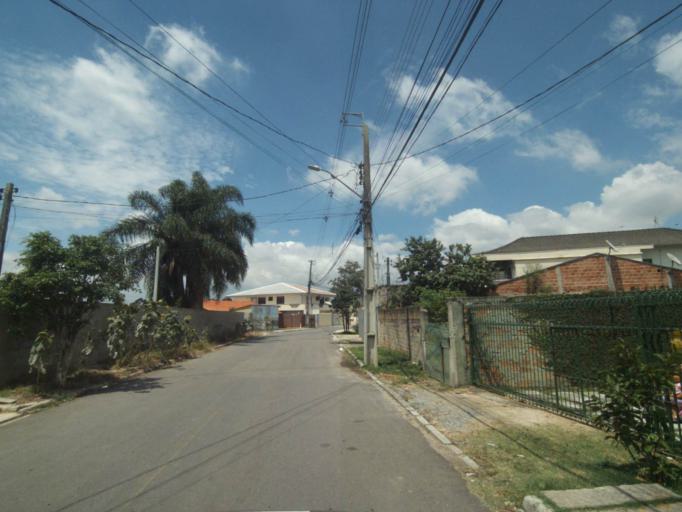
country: BR
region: Parana
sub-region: Pinhais
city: Pinhais
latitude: -25.4757
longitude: -49.1907
